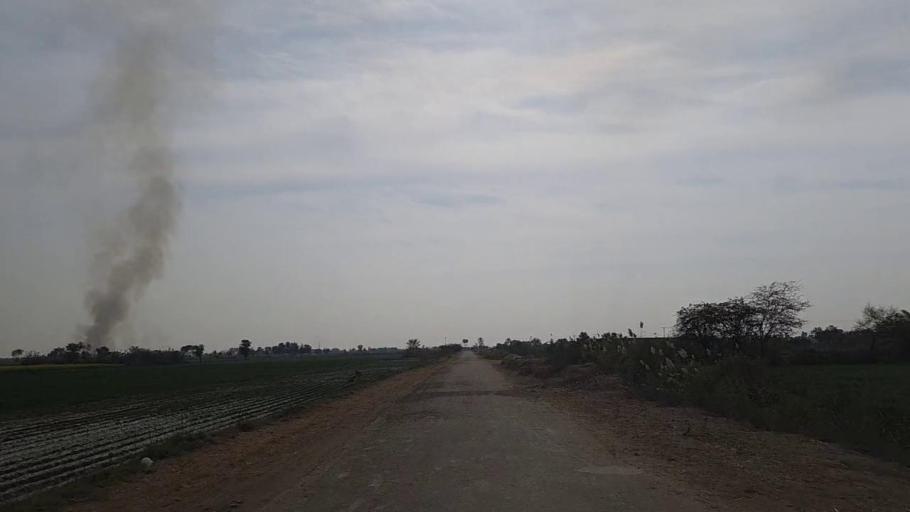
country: PK
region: Sindh
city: Daur
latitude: 26.4554
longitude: 68.4354
